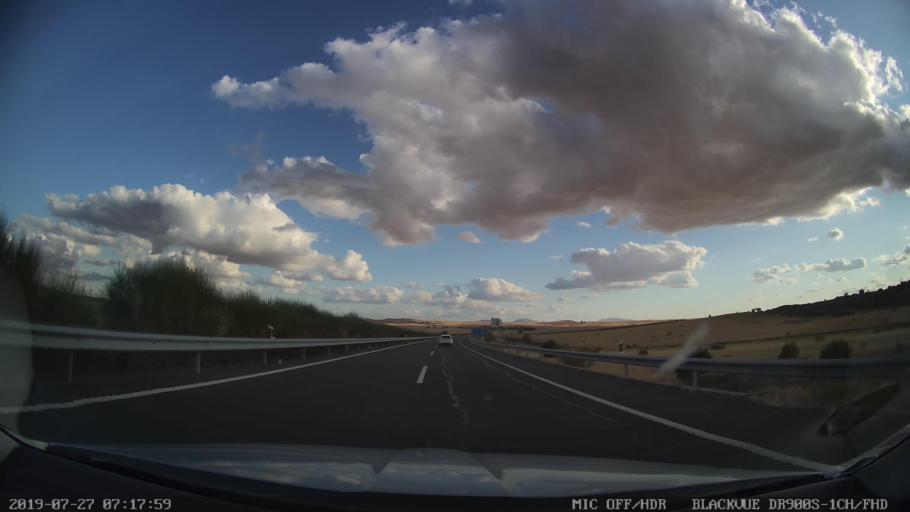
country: ES
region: Extremadura
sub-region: Provincia de Caceres
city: Trujillo
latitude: 39.4263
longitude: -5.8799
